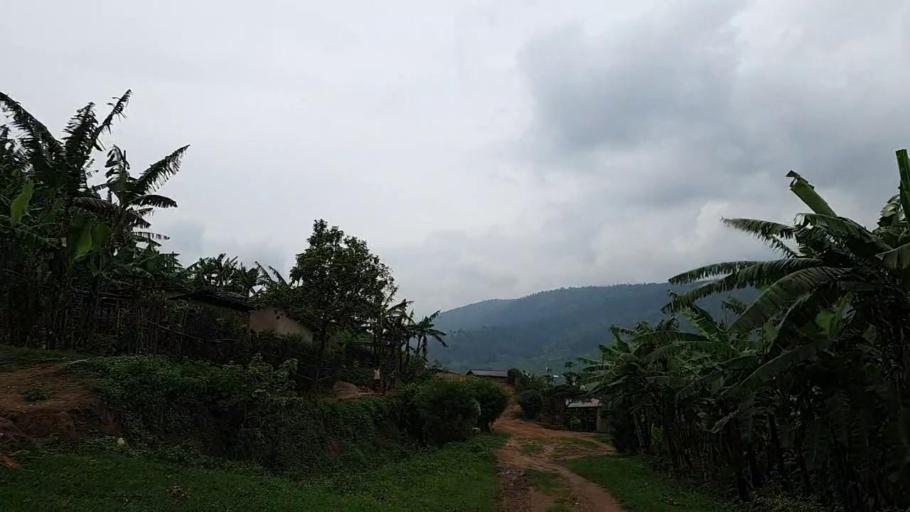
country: RW
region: Kigali
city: Kigali
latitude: -1.9026
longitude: 29.9551
